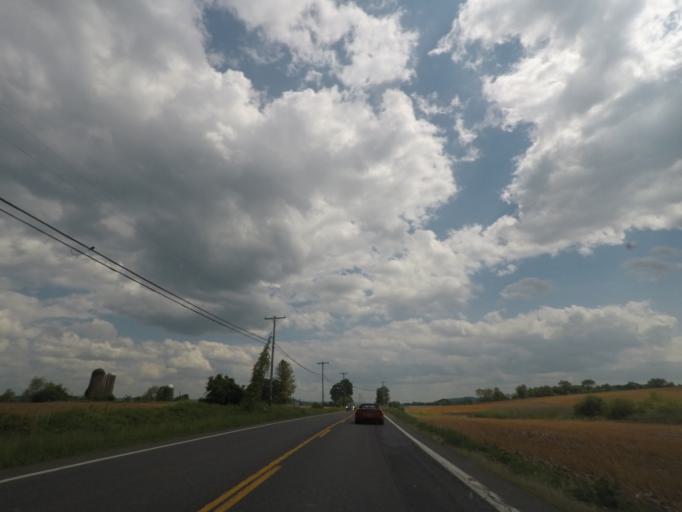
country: US
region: New York
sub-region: Dutchess County
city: Pine Plains
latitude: 41.8949
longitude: -73.5319
